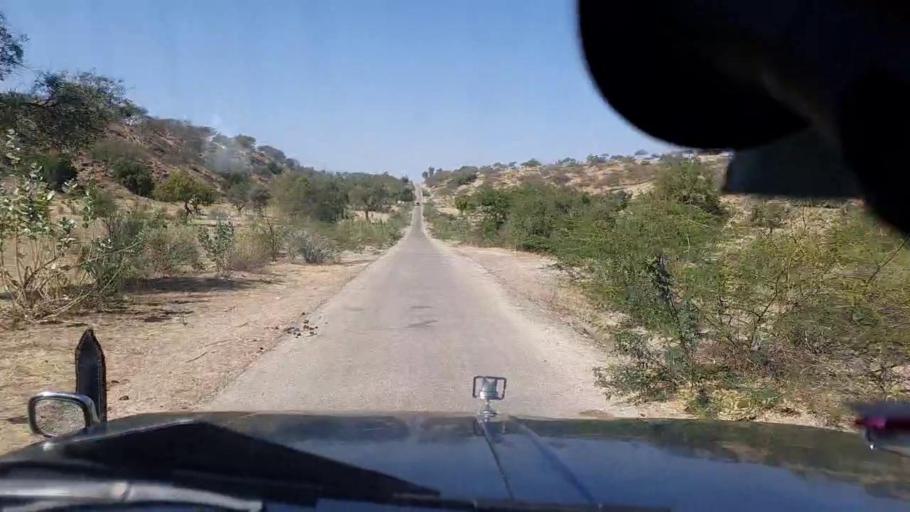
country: PK
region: Sindh
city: Mithi
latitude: 24.6121
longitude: 69.7145
